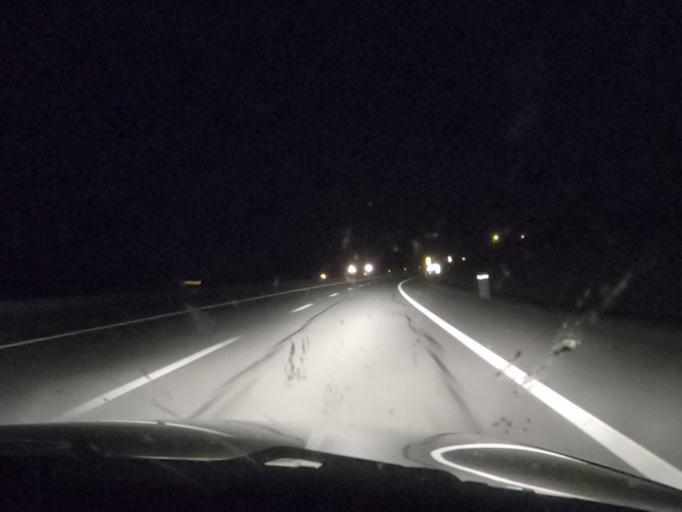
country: PT
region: Evora
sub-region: Estremoz
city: Estremoz
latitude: 38.8385
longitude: -7.6128
